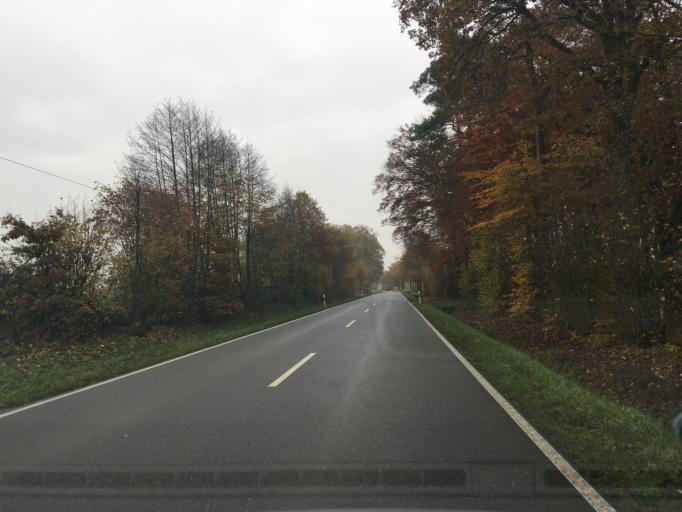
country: DE
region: North Rhine-Westphalia
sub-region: Regierungsbezirk Munster
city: Gescher
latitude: 52.0027
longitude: 7.0252
